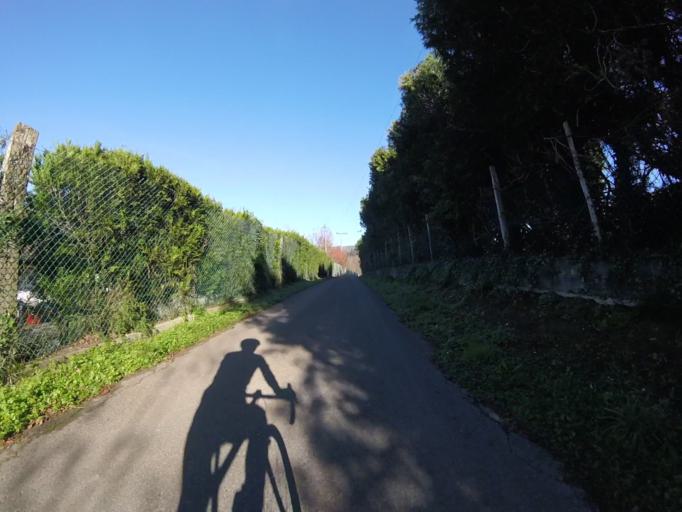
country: ES
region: Basque Country
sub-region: Provincia de Guipuzcoa
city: Usurbil
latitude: 43.2757
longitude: -2.0689
